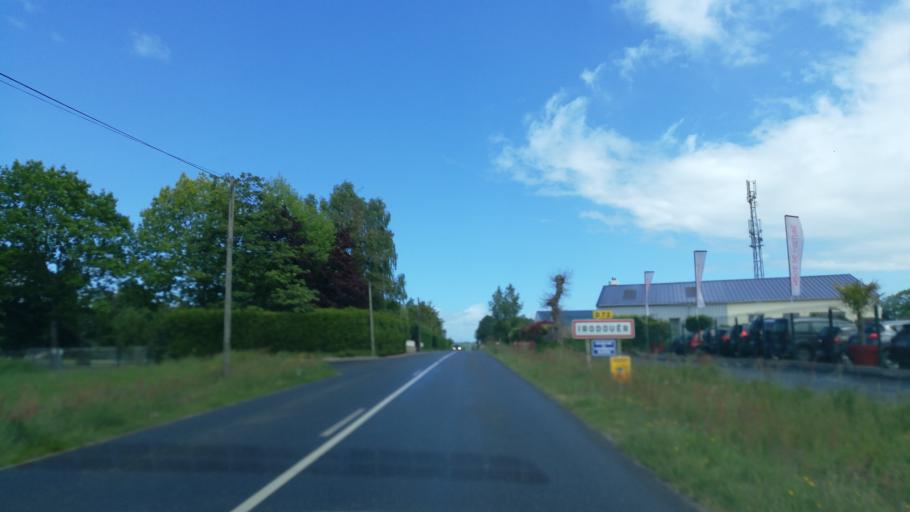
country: FR
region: Brittany
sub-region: Departement d'Ille-et-Vilaine
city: Irodouer
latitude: 48.2417
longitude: -1.9483
